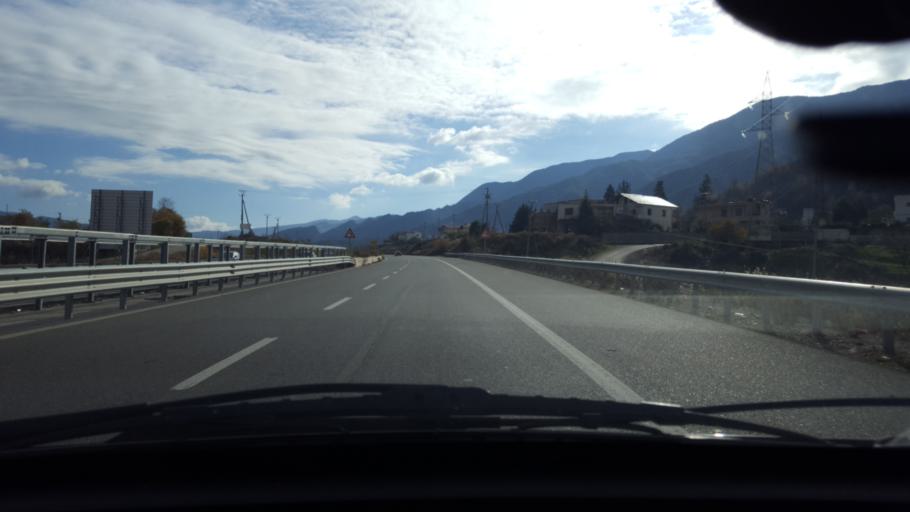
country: AL
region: Tirane
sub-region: Rrethi i Tiranes
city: Berzhite
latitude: 41.2545
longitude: 19.8934
